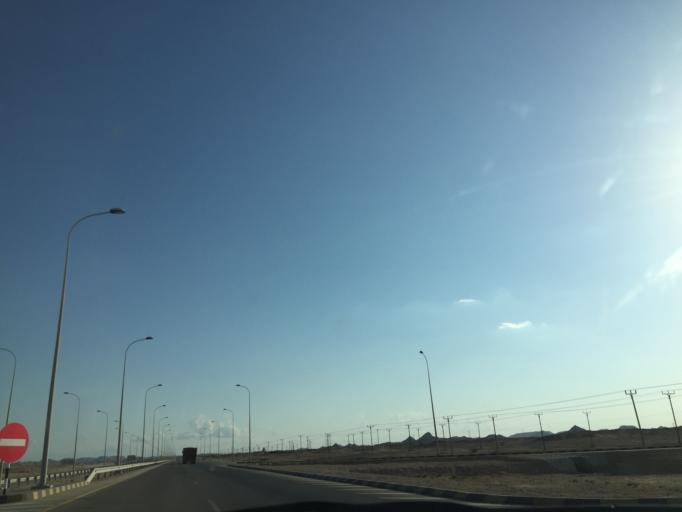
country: OM
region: Zufar
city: Salalah
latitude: 17.5319
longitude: 54.0556
